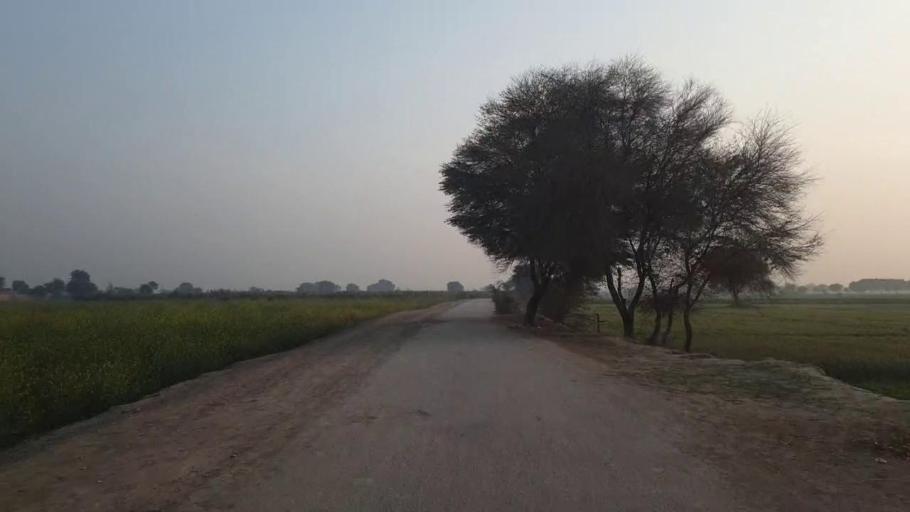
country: PK
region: Sindh
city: Bhit Shah
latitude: 25.7759
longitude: 68.4621
